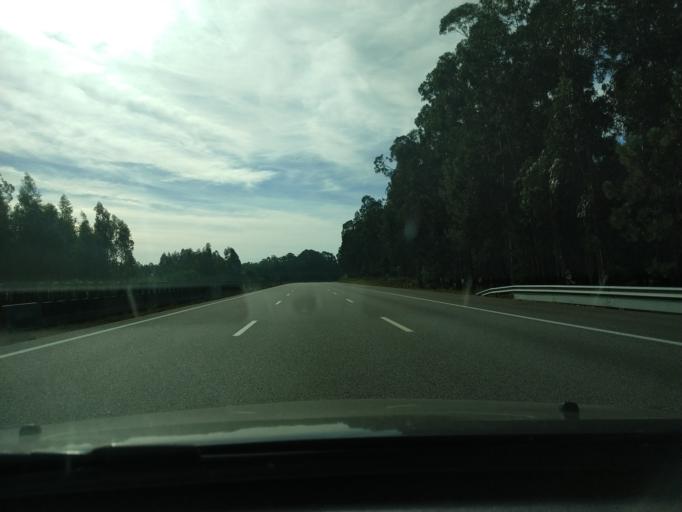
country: PT
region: Aveiro
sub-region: Ovar
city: Valega
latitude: 40.8610
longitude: -8.5573
